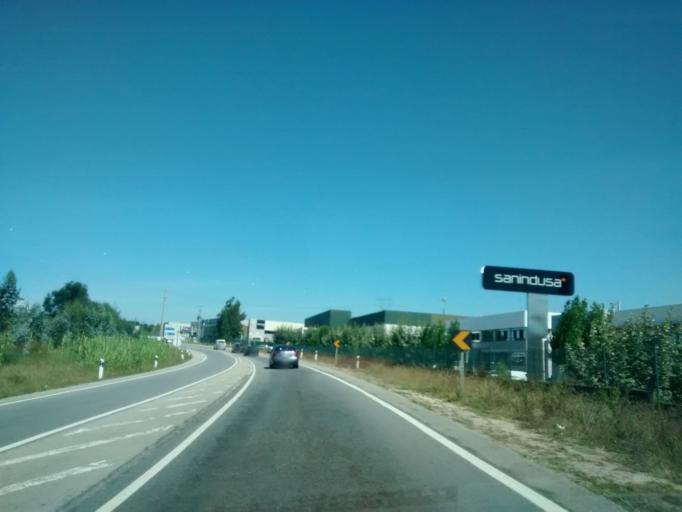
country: PT
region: Aveiro
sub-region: Oliveira do Bairro
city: Oia
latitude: 40.5656
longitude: -8.5642
